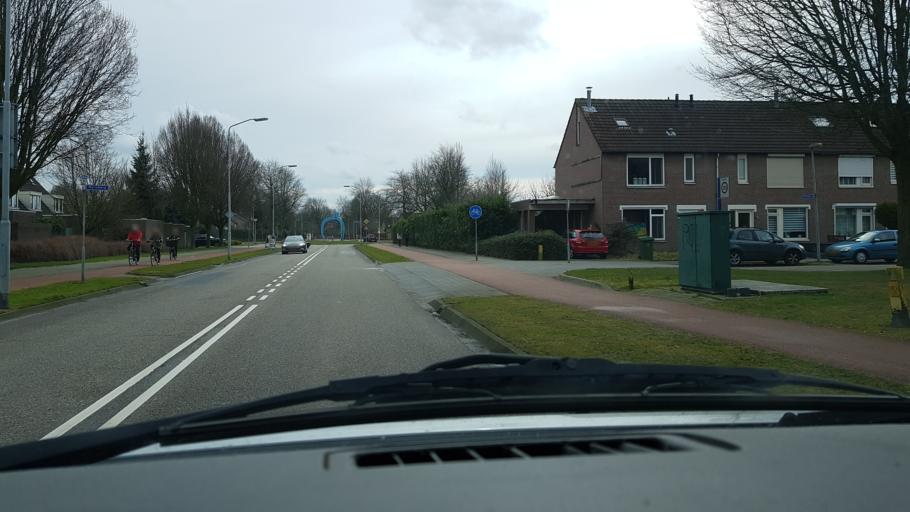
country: NL
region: North Brabant
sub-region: Gemeente Veldhoven
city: Veldhoven
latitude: 51.4260
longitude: 5.3925
